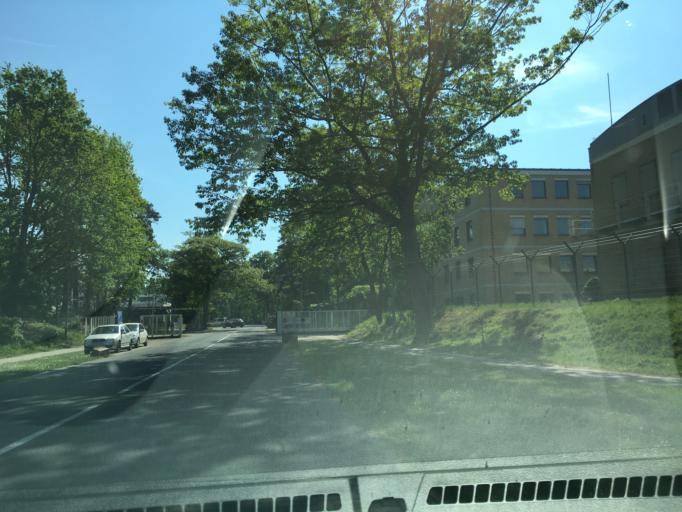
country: DE
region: Lower Saxony
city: Braunschweig
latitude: 52.3146
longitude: 10.5599
